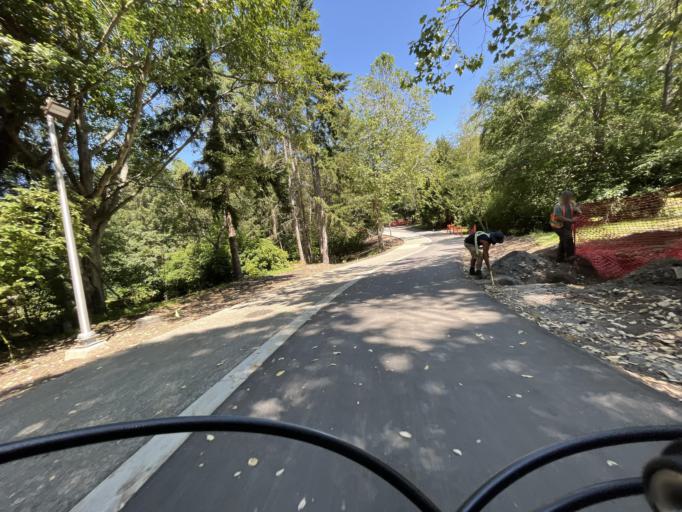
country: CA
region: British Columbia
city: Oak Bay
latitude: 48.4632
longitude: -123.3177
